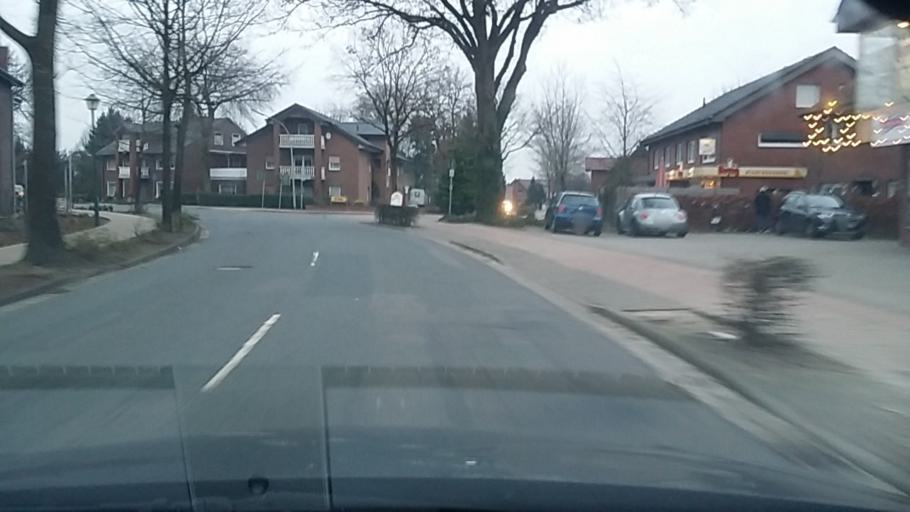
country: DE
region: Lower Saxony
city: Twist
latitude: 52.6363
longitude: 7.0620
